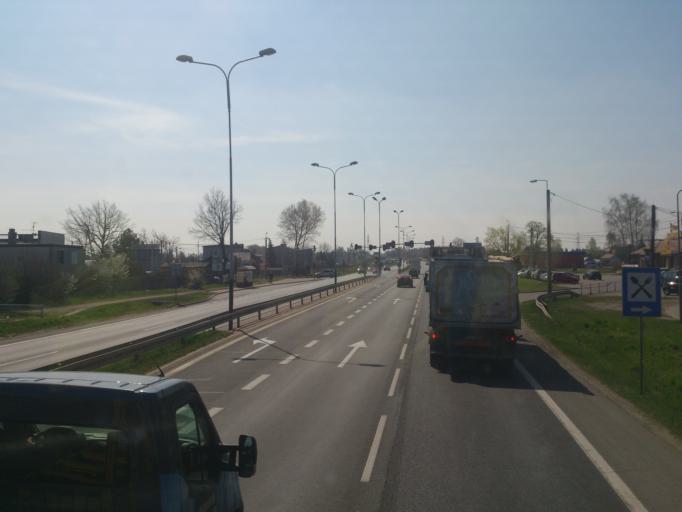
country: PL
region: Lodz Voivodeship
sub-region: Powiat lodzki wschodni
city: Starowa Gora
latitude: 51.6919
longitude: 19.4773
